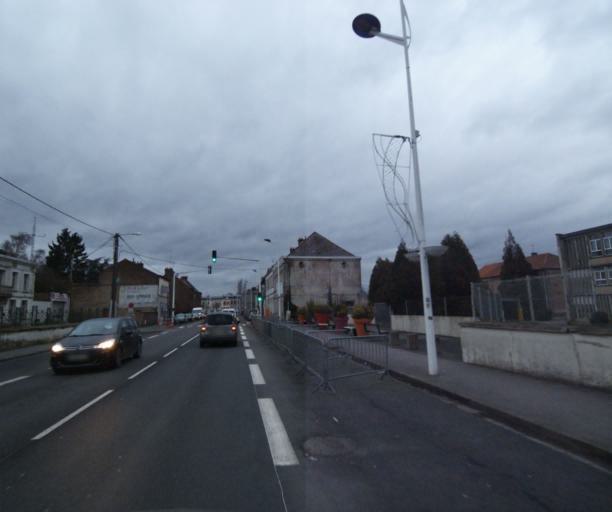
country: FR
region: Nord-Pas-de-Calais
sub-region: Departement du Nord
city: Raismes
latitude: 50.3913
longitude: 3.4854
